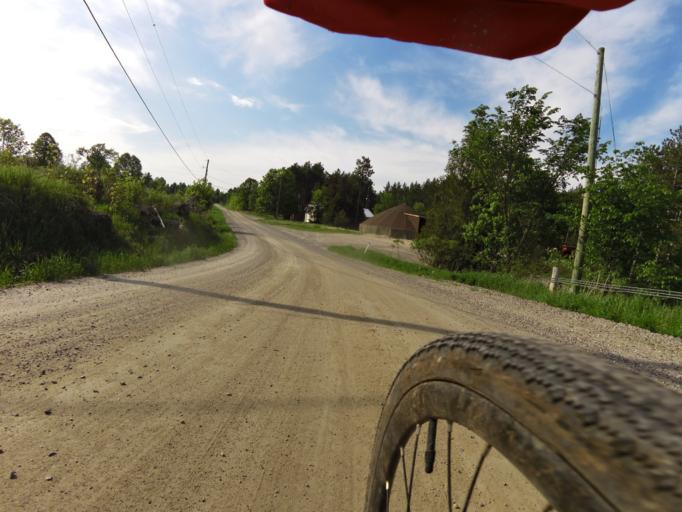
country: CA
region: Ontario
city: Arnprior
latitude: 45.1737
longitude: -76.4697
